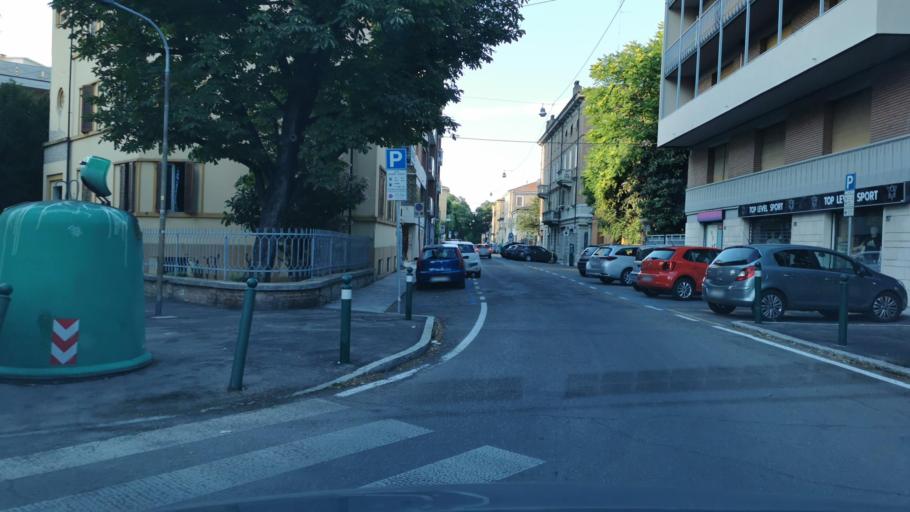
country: IT
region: Emilia-Romagna
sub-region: Provincia di Modena
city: Modena
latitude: 44.6391
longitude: 10.9294
